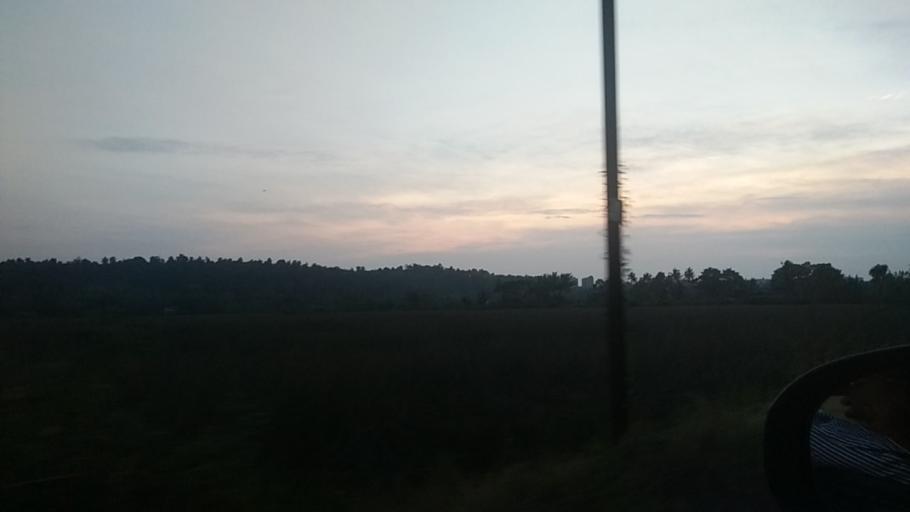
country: IN
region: Goa
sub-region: North Goa
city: Taleigao
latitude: 15.4711
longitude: 73.8350
